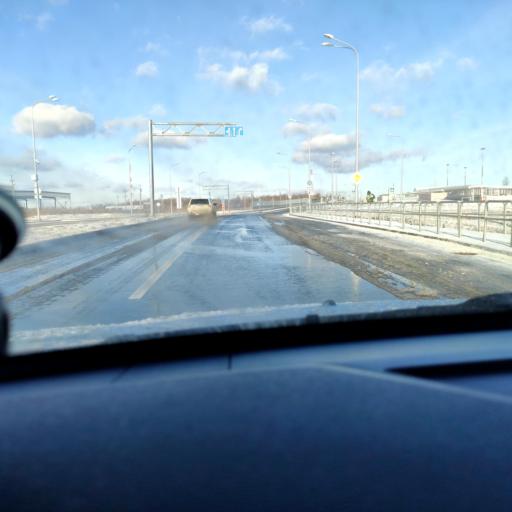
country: RU
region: Samara
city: Samara
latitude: 53.2750
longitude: 50.2317
